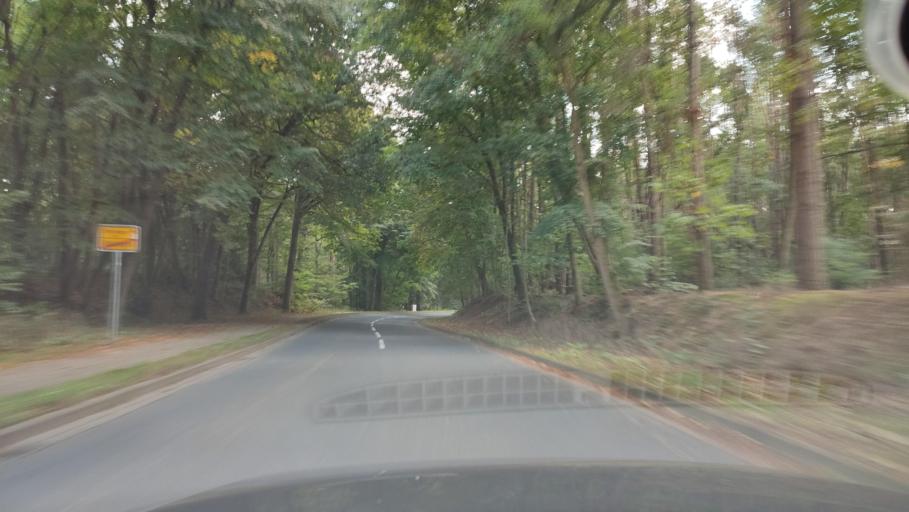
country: DE
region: Lower Saxony
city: Bomlitz
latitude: 52.8816
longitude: 9.6551
